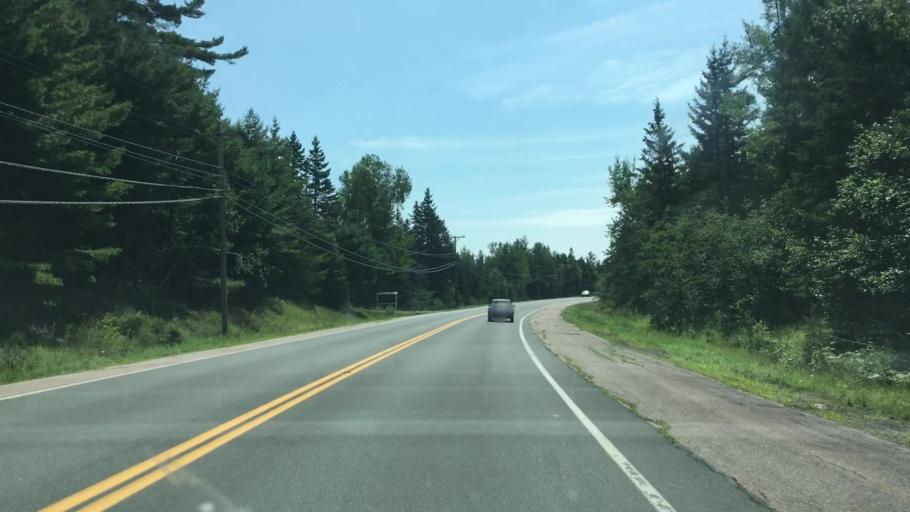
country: US
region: Maine
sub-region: Washington County
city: Calais
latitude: 45.1539
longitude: -67.1756
